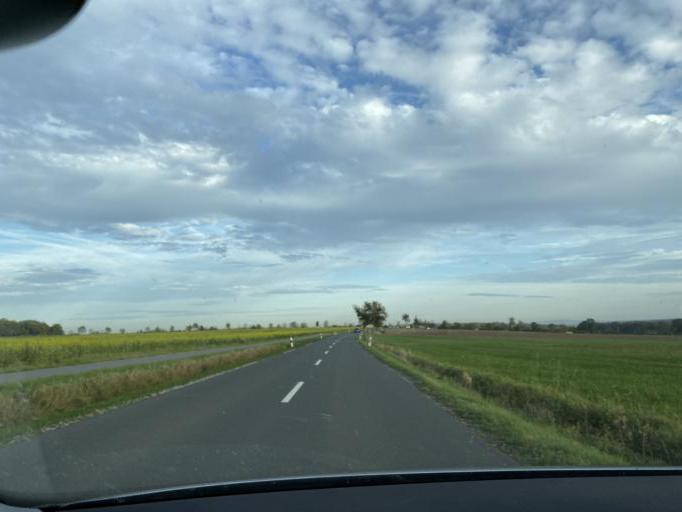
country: DE
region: Bavaria
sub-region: Regierungsbezirk Mittelfranken
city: Puschendorf
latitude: 49.5323
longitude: 10.8068
